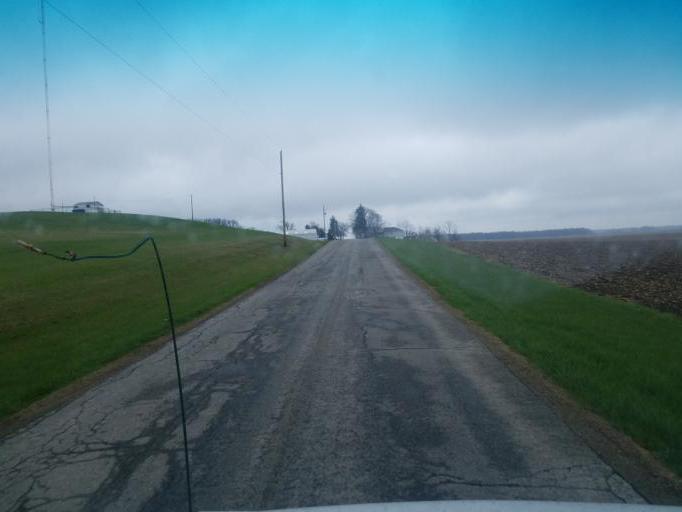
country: US
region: Ohio
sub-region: Huron County
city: Plymouth
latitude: 40.9450
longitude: -82.6623
